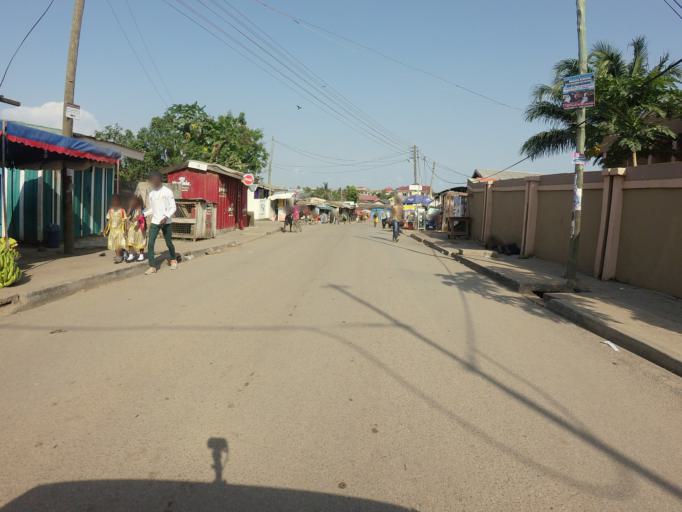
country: GH
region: Greater Accra
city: Dome
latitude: 5.6099
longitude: -0.2488
